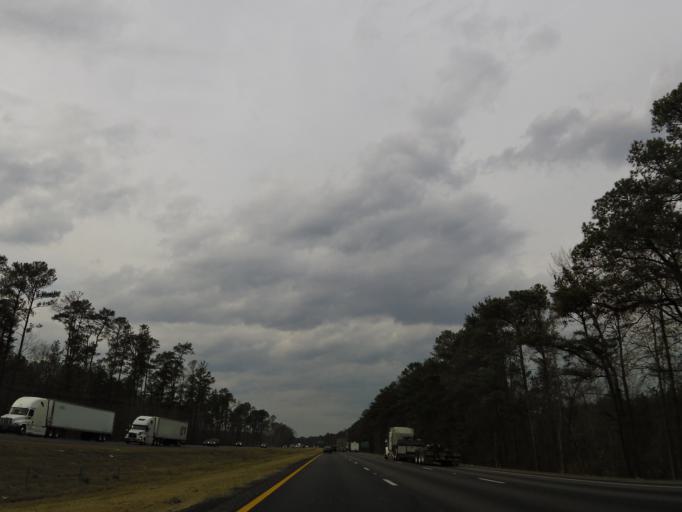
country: US
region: South Carolina
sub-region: Lexington County
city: Pineridge
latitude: 33.9026
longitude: -81.0494
